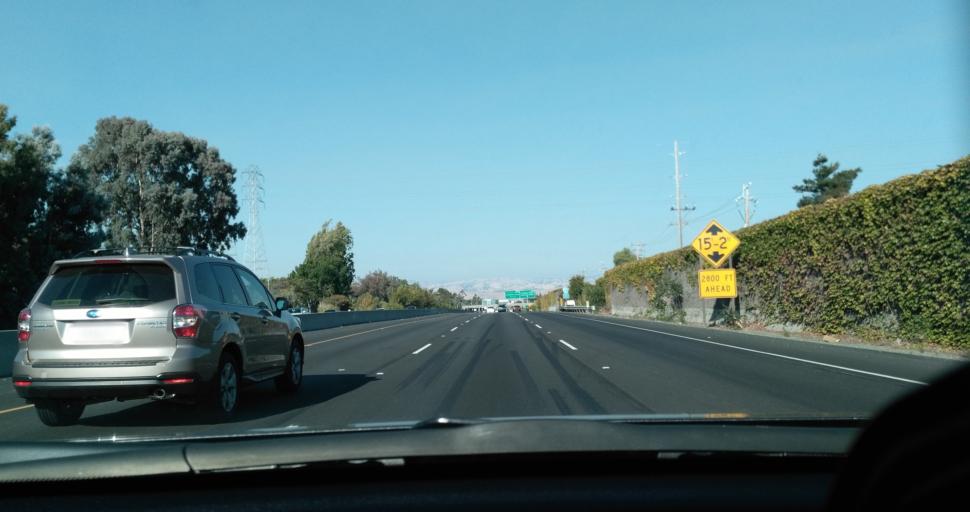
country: US
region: California
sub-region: Santa Clara County
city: Sunnyvale
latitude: 37.4072
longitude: -122.0077
